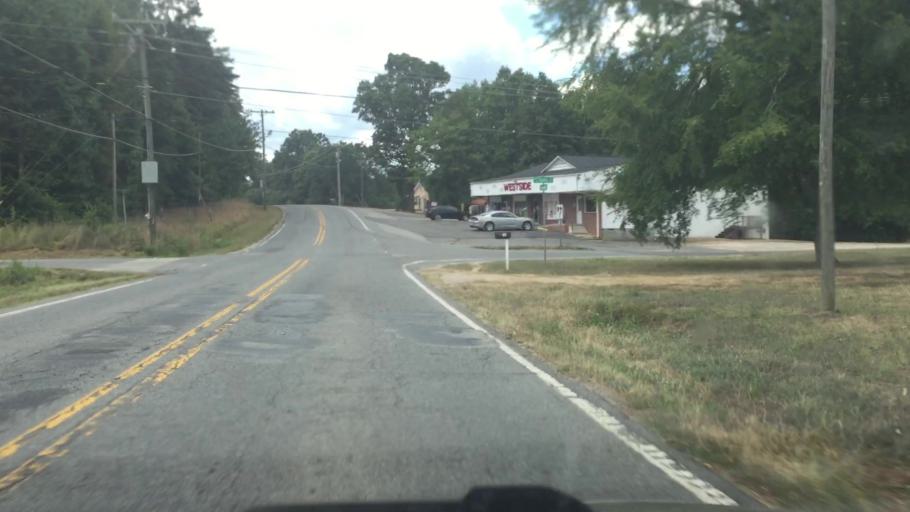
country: US
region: North Carolina
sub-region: Rowan County
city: Enochville
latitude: 35.5280
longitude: -80.6687
